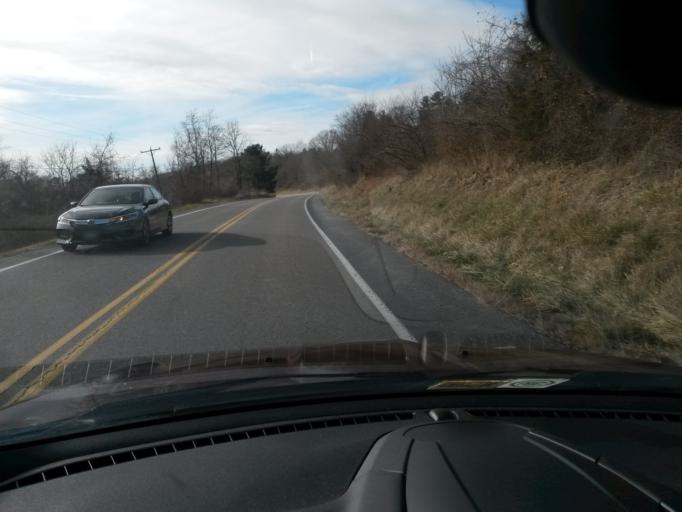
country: US
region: Virginia
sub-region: Augusta County
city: Jolivue
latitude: 38.1123
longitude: -79.3004
